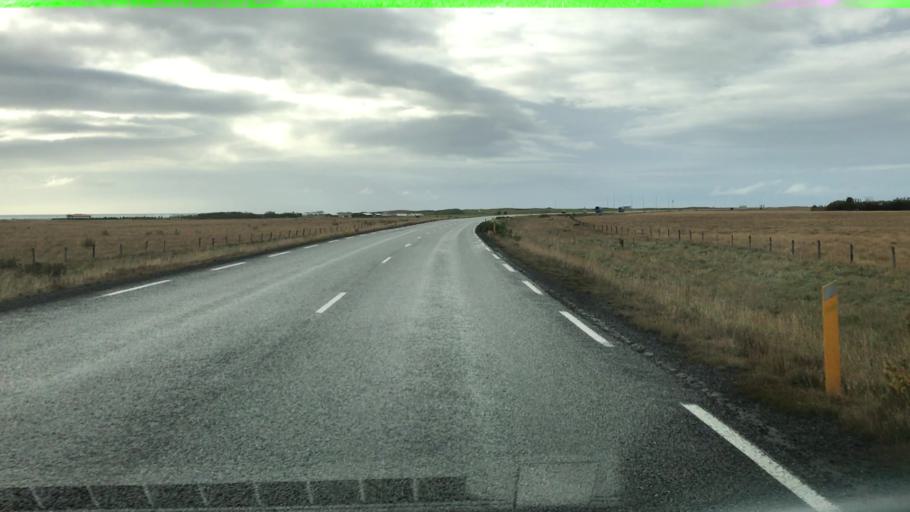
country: IS
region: West
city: Akranes
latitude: 64.3091
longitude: -21.9760
